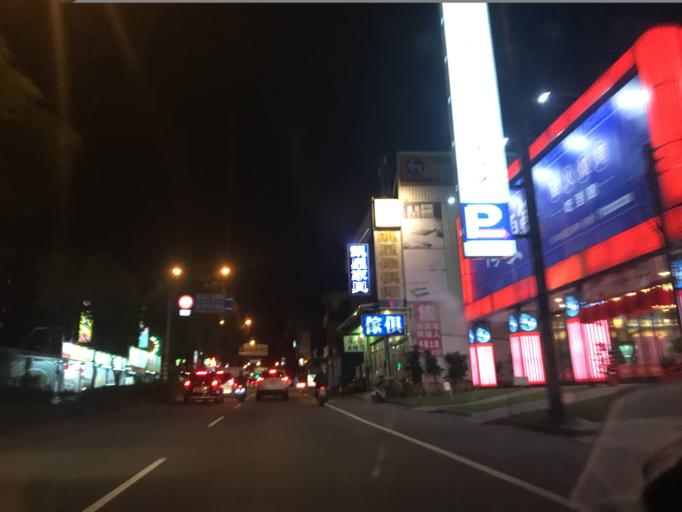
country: TW
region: Taiwan
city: Daxi
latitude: 24.8721
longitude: 121.2137
